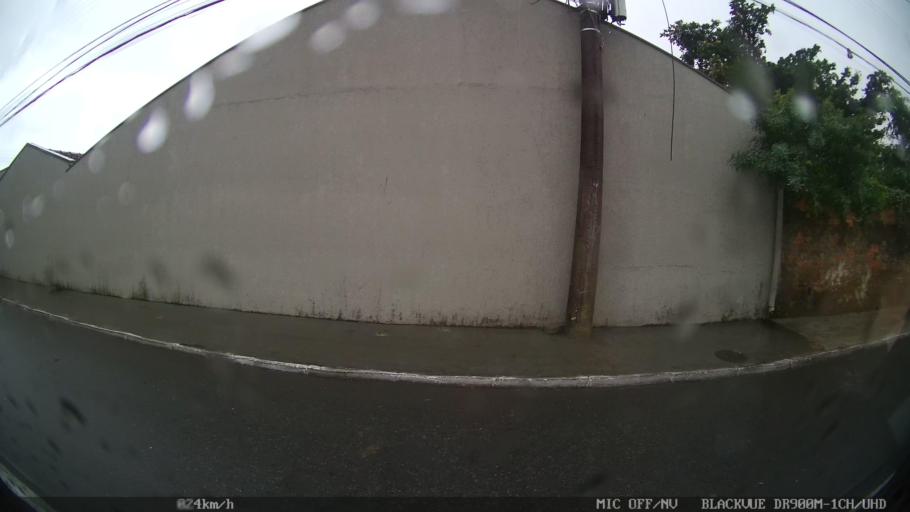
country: BR
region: Santa Catarina
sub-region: Itajai
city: Itajai
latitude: -26.9158
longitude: -48.6670
